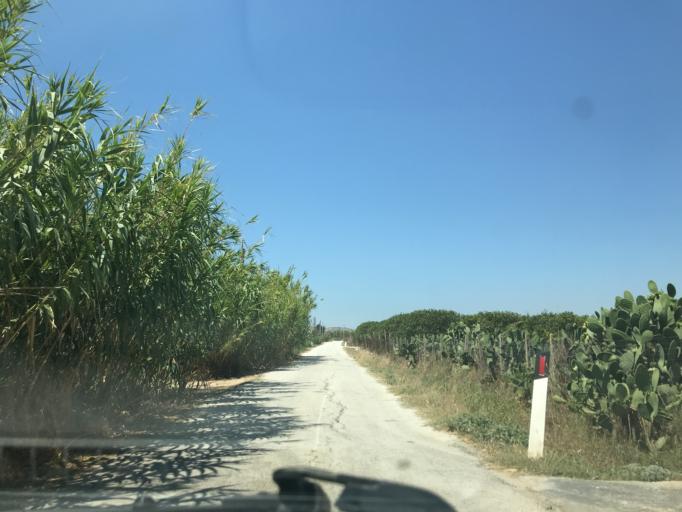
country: IT
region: Sicily
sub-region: Provincia di Siracusa
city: Noto
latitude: 36.8330
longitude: 15.0432
